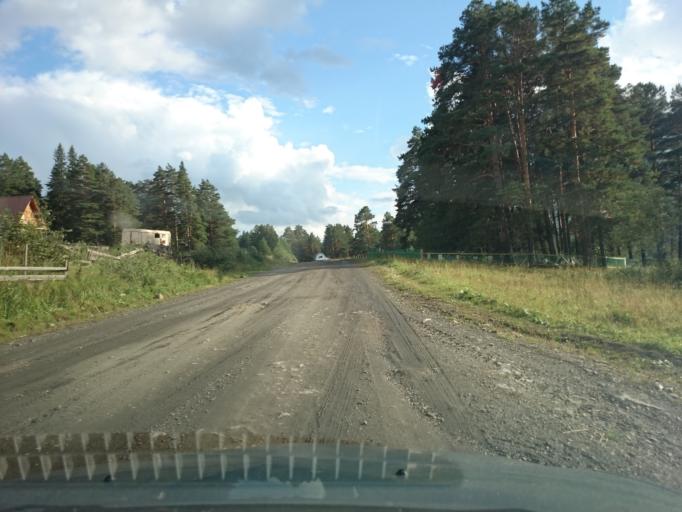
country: RU
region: Bashkortostan
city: Beloretsk
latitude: 54.0452
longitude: 58.3308
